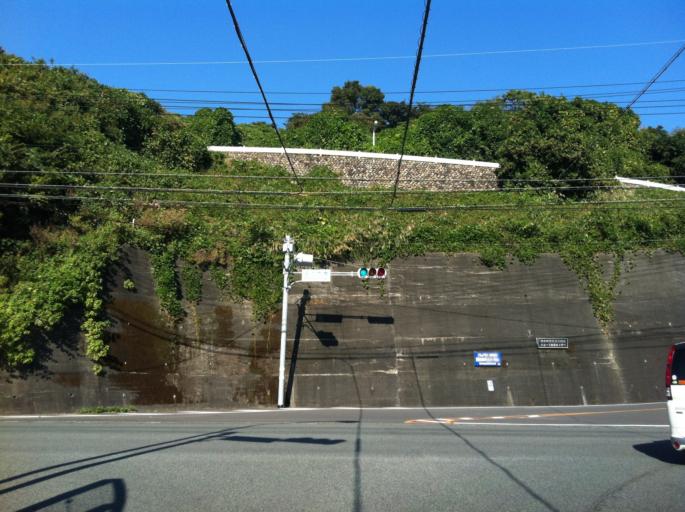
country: JP
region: Shizuoka
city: Fuji
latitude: 35.1255
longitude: 138.6168
